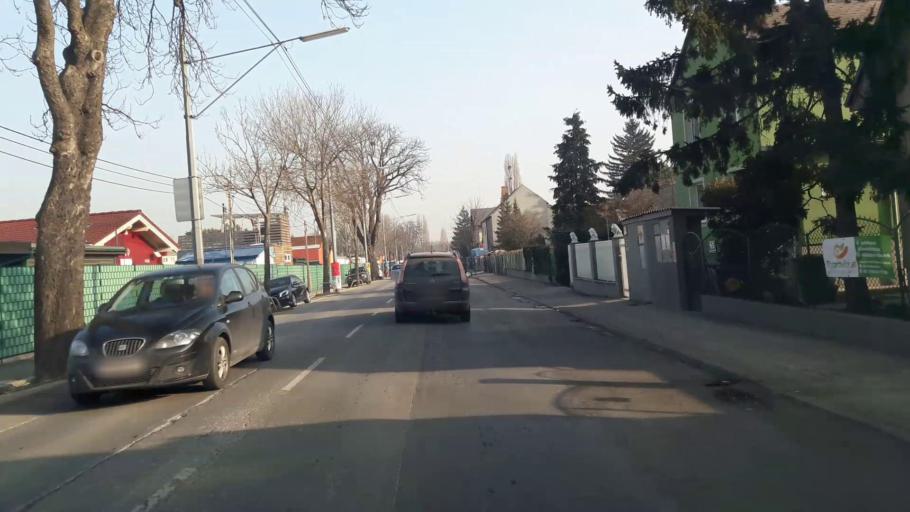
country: AT
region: Lower Austria
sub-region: Politischer Bezirk Modling
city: Vosendorf
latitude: 48.1522
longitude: 16.3248
